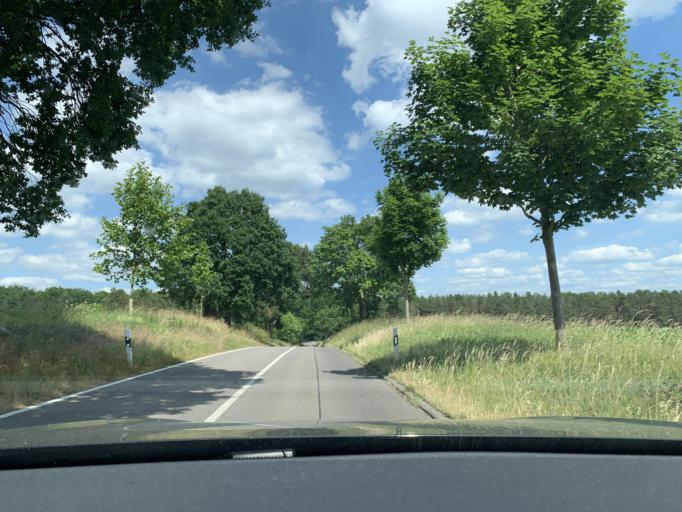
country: DE
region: Brandenburg
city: Rheinsberg
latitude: 53.1669
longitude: 12.7757
